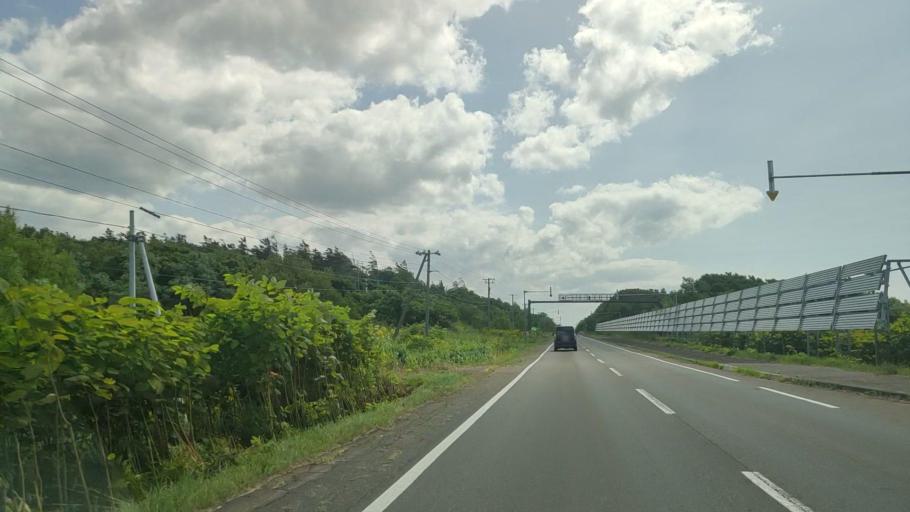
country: JP
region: Hokkaido
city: Makubetsu
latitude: 44.7690
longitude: 141.7928
